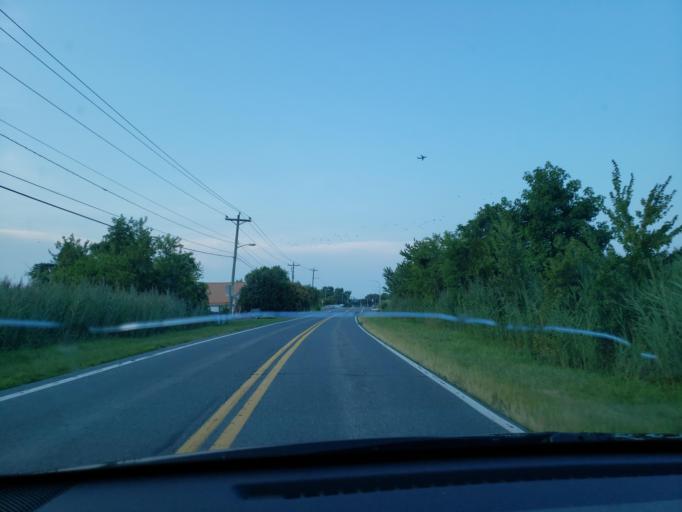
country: US
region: Delaware
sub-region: Kent County
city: Riverview
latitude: 39.0117
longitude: -75.4644
